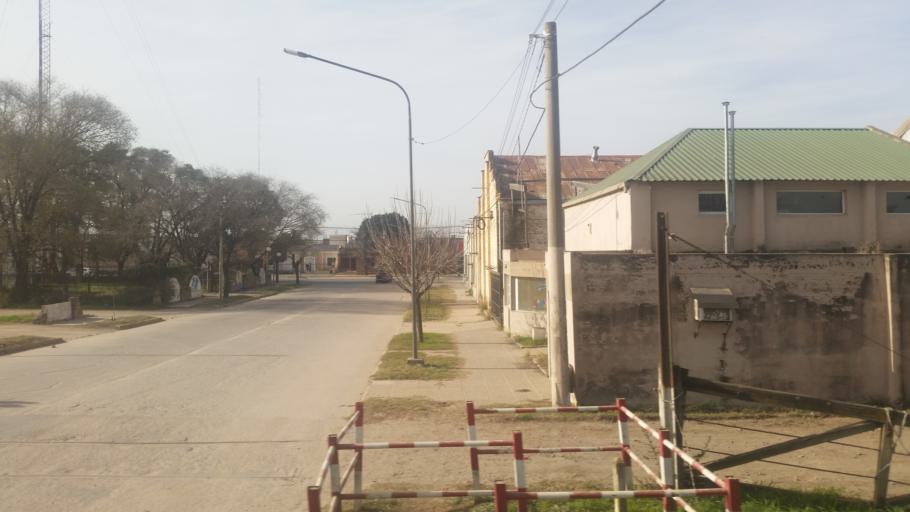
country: AR
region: Cordoba
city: Laguna Larga
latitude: -31.7796
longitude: -63.8005
